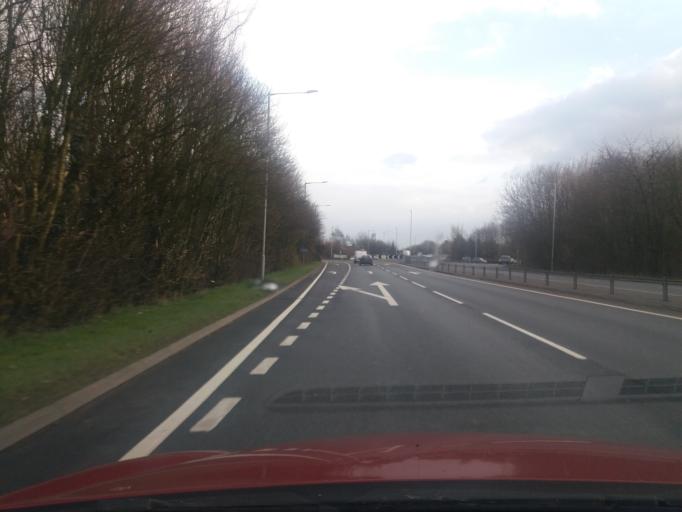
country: GB
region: England
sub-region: Lancashire
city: Clayton-le-Woods
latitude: 53.7304
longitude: -2.6749
